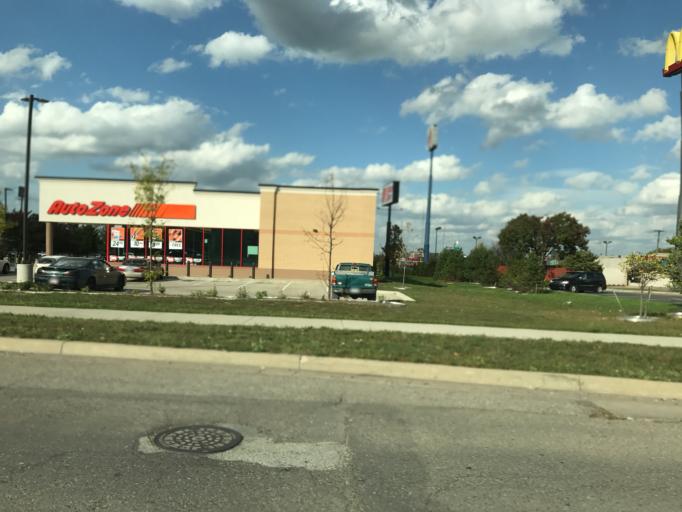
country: US
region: Michigan
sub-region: Oakland County
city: Wixom
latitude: 42.4947
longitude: -83.5374
